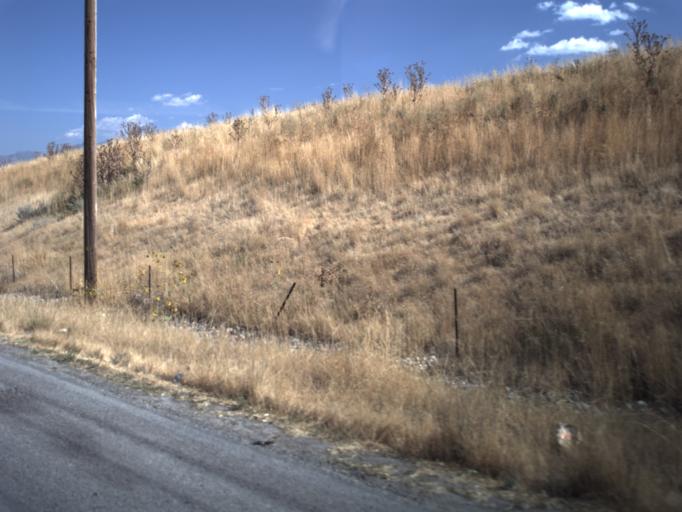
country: US
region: Utah
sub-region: Cache County
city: Hyrum
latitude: 41.6440
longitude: -111.8326
